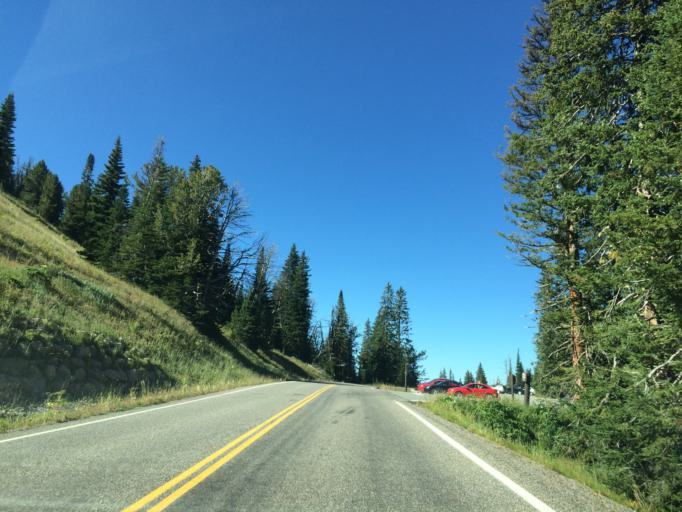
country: US
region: Montana
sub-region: Gallatin County
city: West Yellowstone
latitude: 44.7840
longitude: -110.4539
